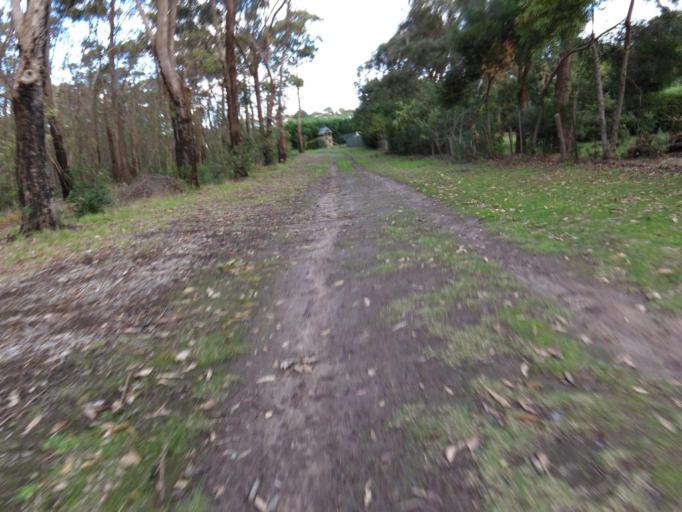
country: AU
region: Victoria
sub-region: Yarra Ranges
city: Lysterfield
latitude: -37.9566
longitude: 145.2865
